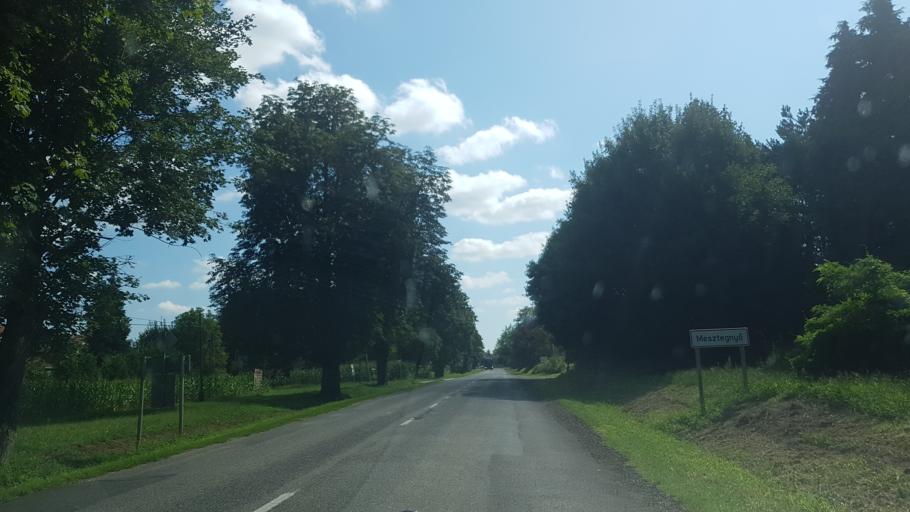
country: HU
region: Somogy
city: Marcali
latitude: 46.5116
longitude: 17.4242
